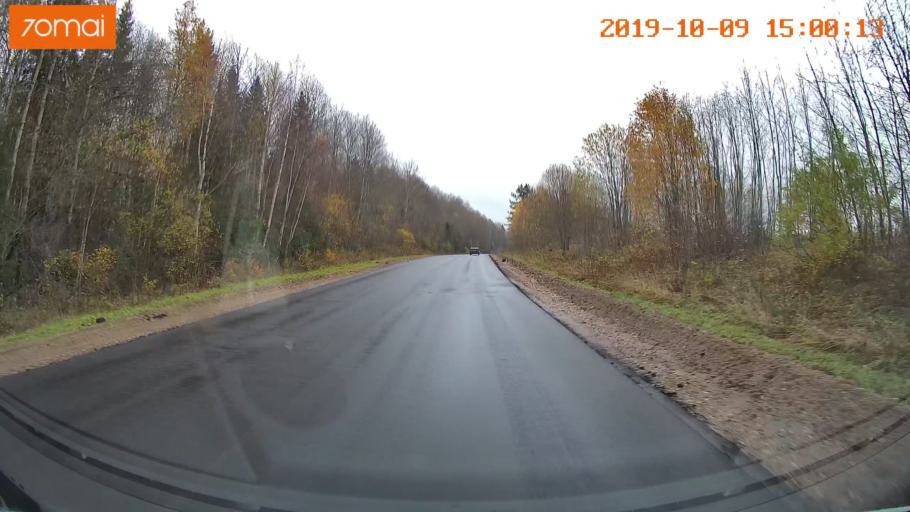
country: RU
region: Kostroma
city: Chistyye Bory
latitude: 58.3118
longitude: 41.6765
